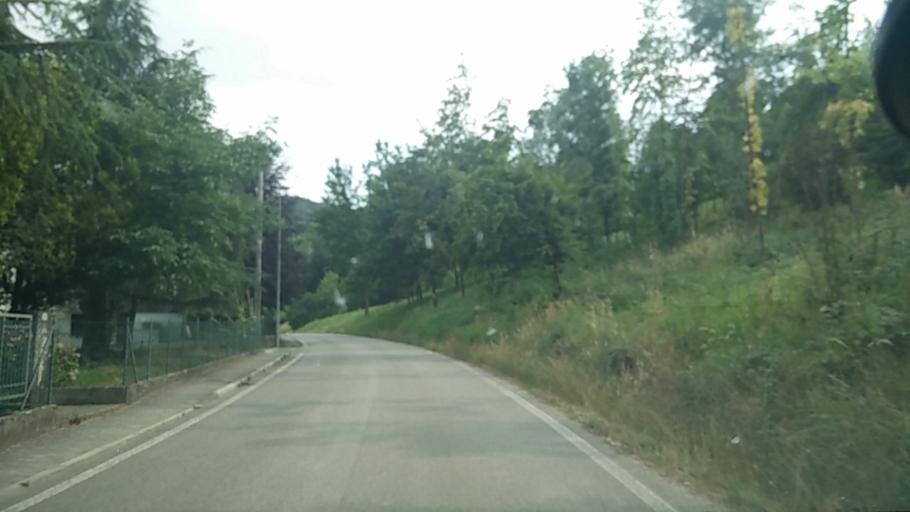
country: IT
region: Veneto
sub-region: Provincia di Treviso
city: Follina
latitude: 45.9343
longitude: 12.1264
